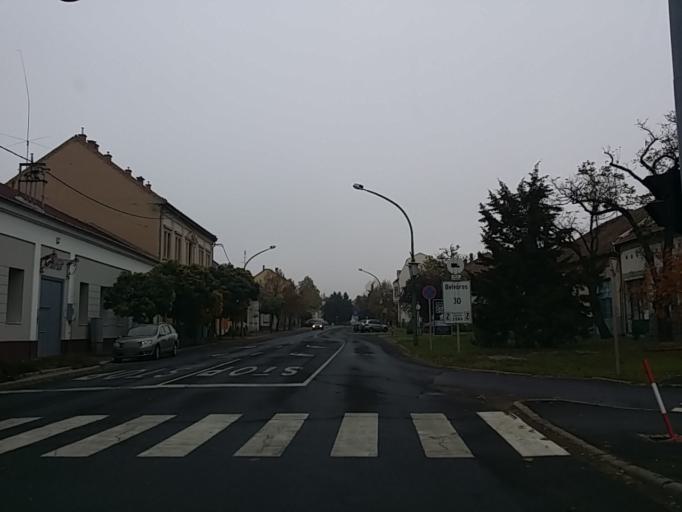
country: HU
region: Heves
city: Gyongyos
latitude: 47.7806
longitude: 19.9233
